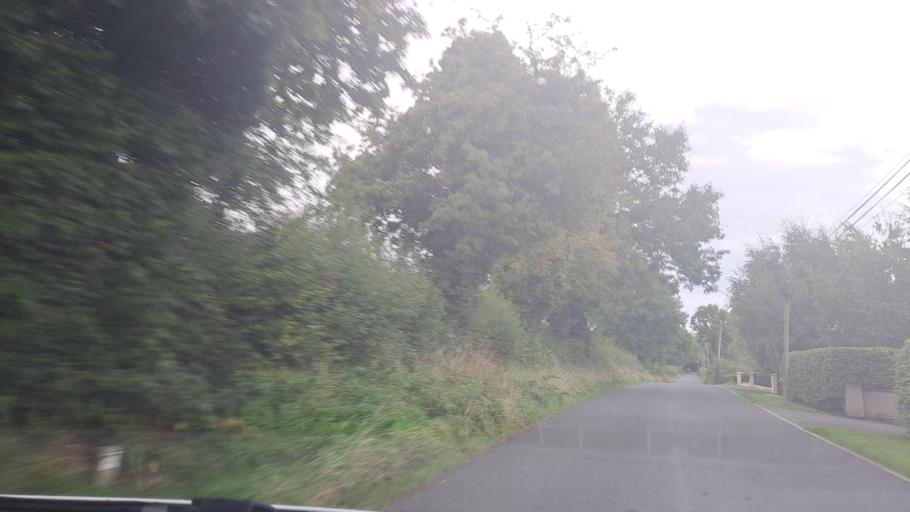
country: IE
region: Ulster
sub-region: County Monaghan
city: Carrickmacross
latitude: 53.9694
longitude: -6.7485
